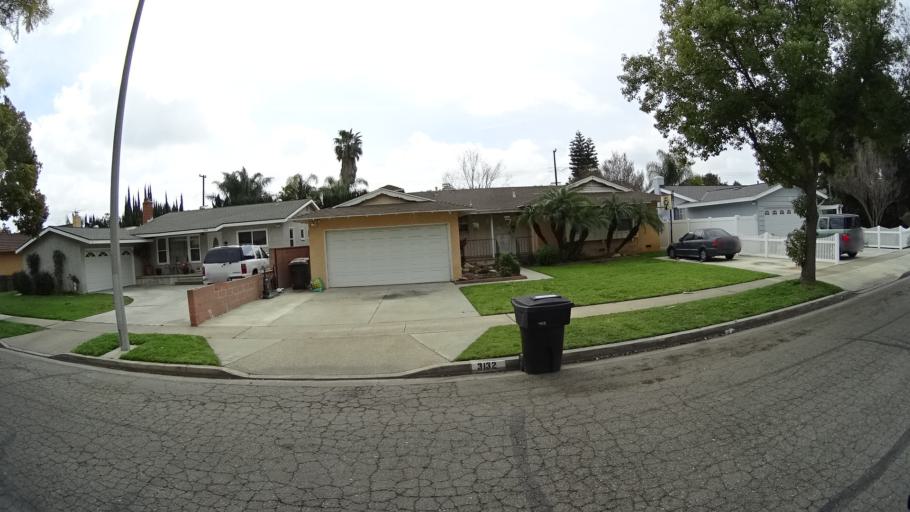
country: US
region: California
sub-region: Orange County
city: Stanton
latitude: 33.8290
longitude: -118.0000
